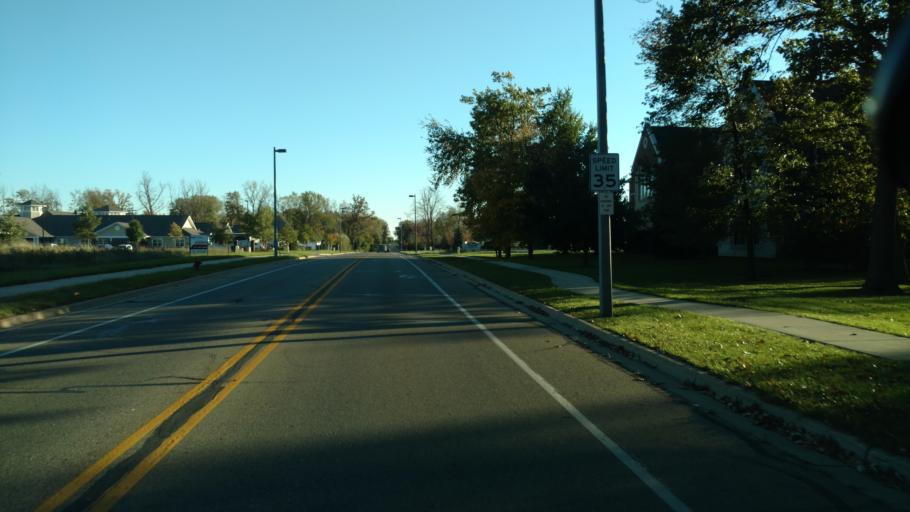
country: US
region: Michigan
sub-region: Ingham County
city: East Lansing
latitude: 42.7724
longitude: -84.5033
